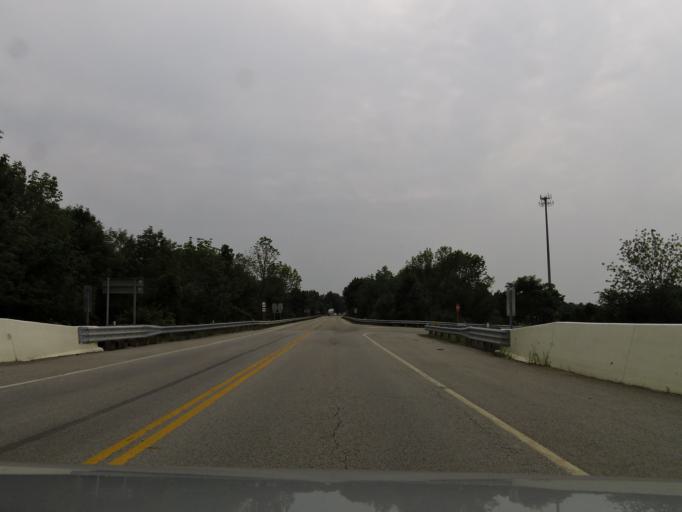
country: US
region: Ohio
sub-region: Clinton County
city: Wilmington
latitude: 39.3615
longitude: -83.8666
